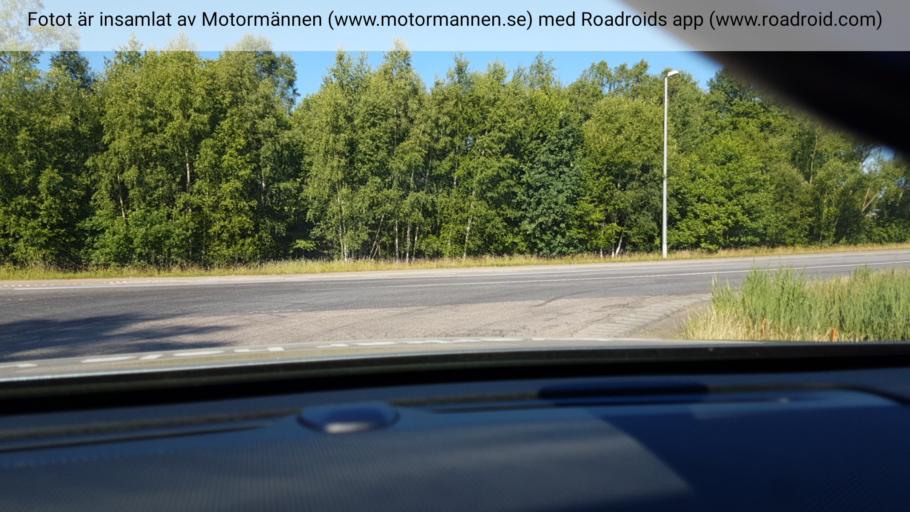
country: SE
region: Kronoberg
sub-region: Markaryds Kommun
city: Markaryd
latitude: 56.4448
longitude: 13.6025
